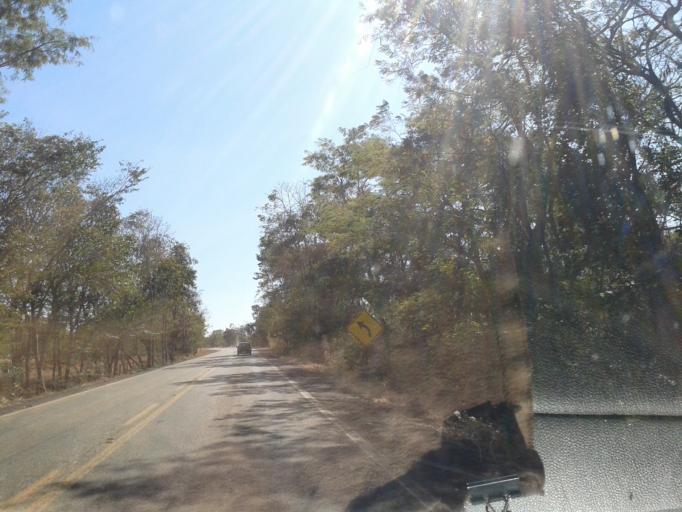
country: BR
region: Goias
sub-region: Crixas
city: Crixas
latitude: -14.0816
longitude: -50.3336
